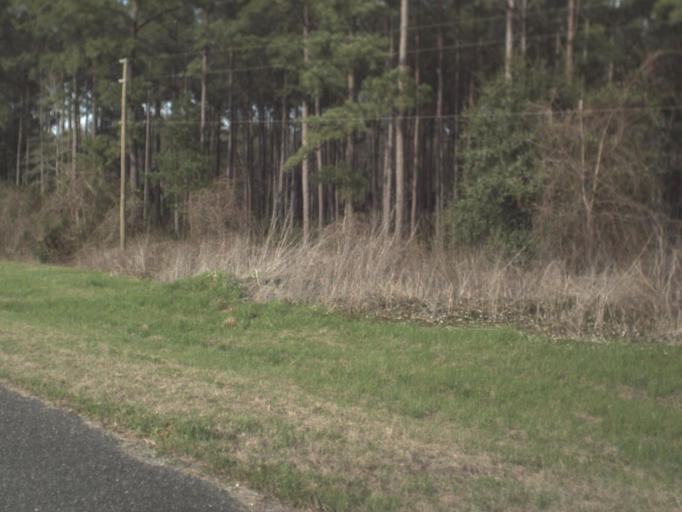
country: US
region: Florida
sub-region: Jefferson County
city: Monticello
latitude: 30.6396
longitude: -83.8740
